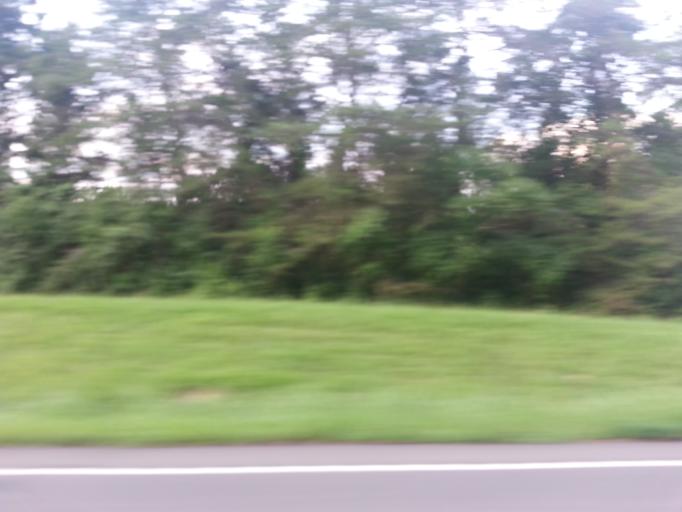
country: US
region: Tennessee
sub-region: Anderson County
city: Norris
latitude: 36.1321
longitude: -84.0065
